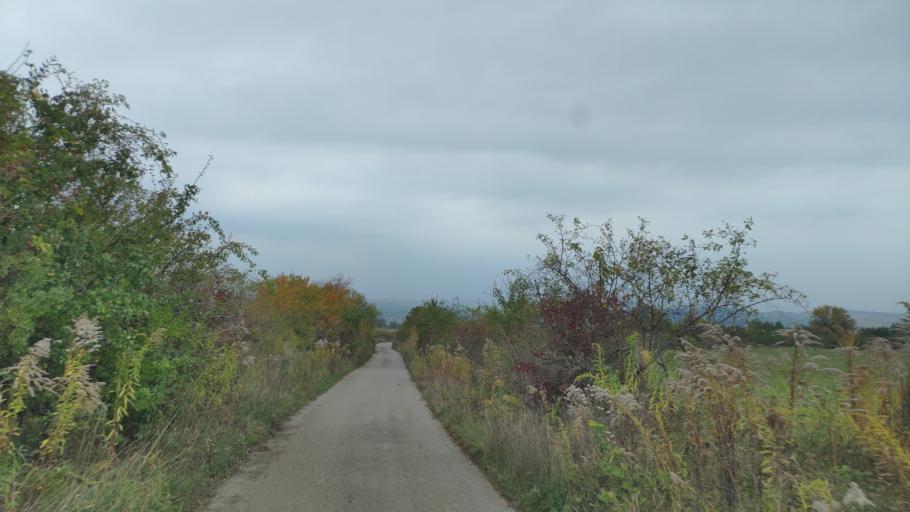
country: SK
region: Kosicky
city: Kosice
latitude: 48.6298
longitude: 21.4025
